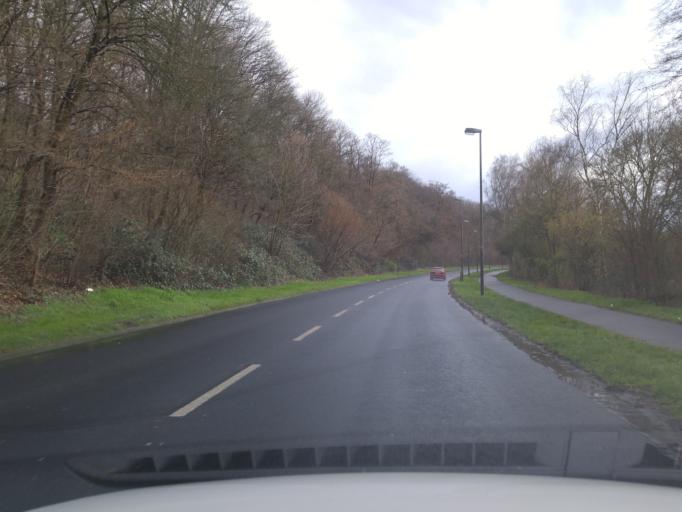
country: DE
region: North Rhine-Westphalia
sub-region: Regierungsbezirk Koln
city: Hoehenberg
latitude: 50.9356
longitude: 7.0317
